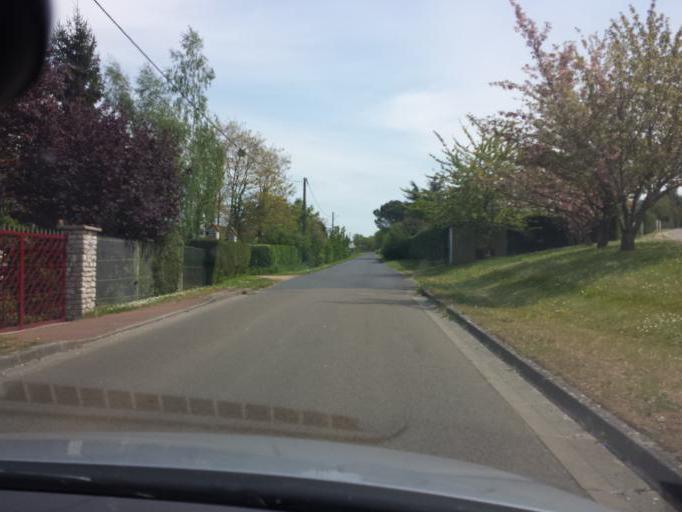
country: FR
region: Centre
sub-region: Departement d'Eure-et-Loir
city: Anet
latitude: 48.8524
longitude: 1.4464
